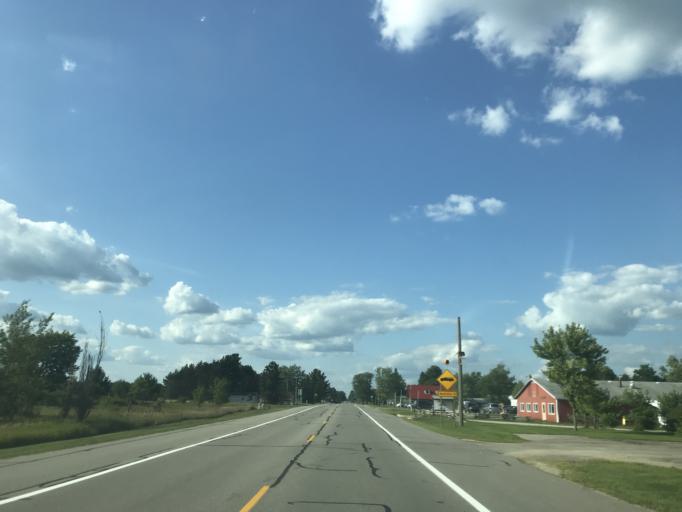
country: US
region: Michigan
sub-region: Newaygo County
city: White Cloud
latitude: 43.5587
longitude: -85.7716
